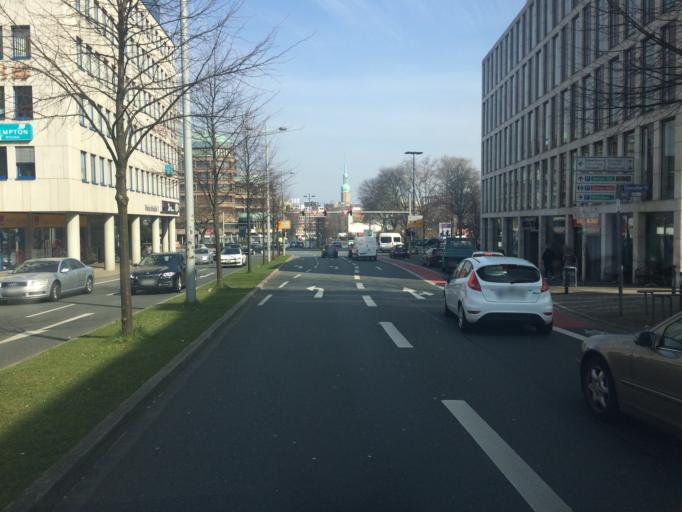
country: DE
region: North Rhine-Westphalia
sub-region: Regierungsbezirk Arnsberg
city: Dortmund
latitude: 51.5093
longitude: 7.4617
